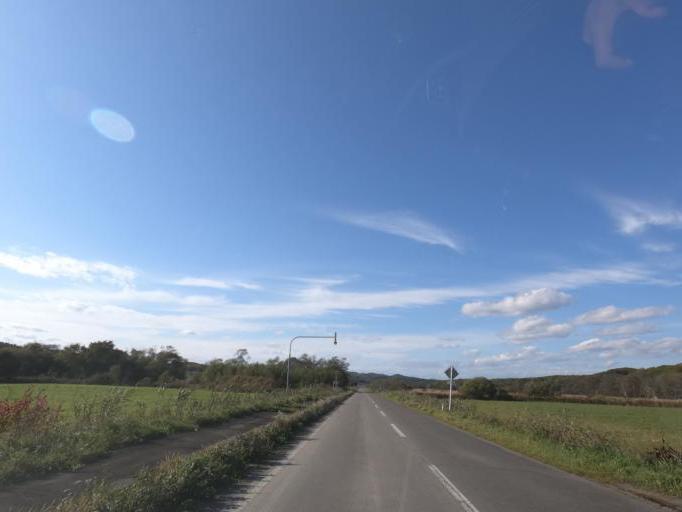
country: JP
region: Hokkaido
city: Obihiro
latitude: 42.6378
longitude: 143.5138
